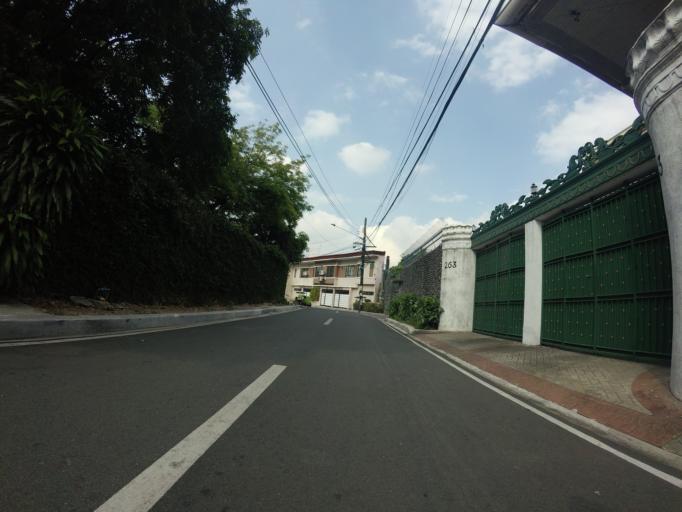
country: PH
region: Metro Manila
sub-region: San Juan
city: San Juan
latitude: 14.6034
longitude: 121.0340
